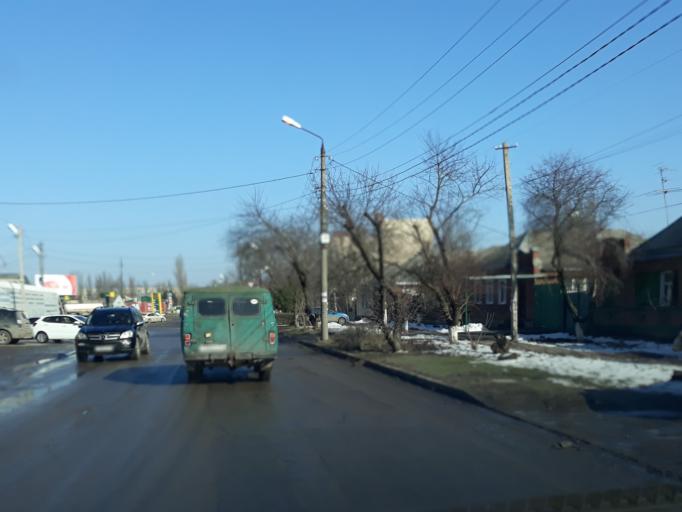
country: RU
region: Rostov
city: Taganrog
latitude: 47.2280
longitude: 38.8762
